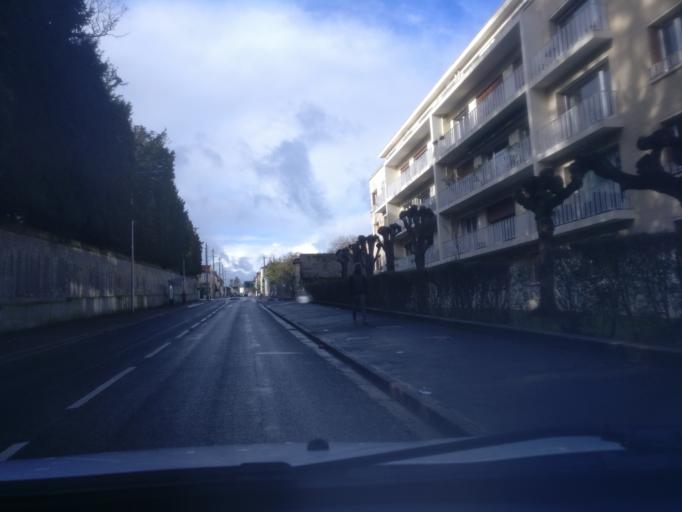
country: FR
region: Lower Normandy
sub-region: Departement du Calvados
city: Caen
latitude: 49.1903
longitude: -0.3722
